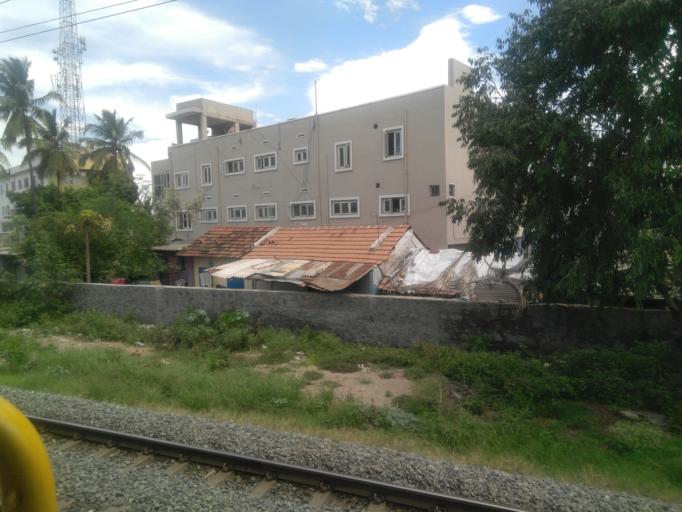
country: IN
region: Tamil Nadu
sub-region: Coimbatore
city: Coimbatore
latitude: 11.0144
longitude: 76.9570
